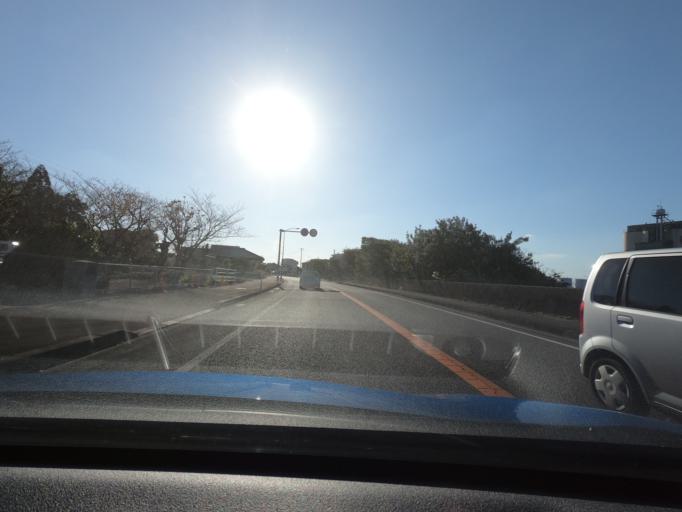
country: JP
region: Kagoshima
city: Izumi
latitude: 32.1302
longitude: 130.3460
